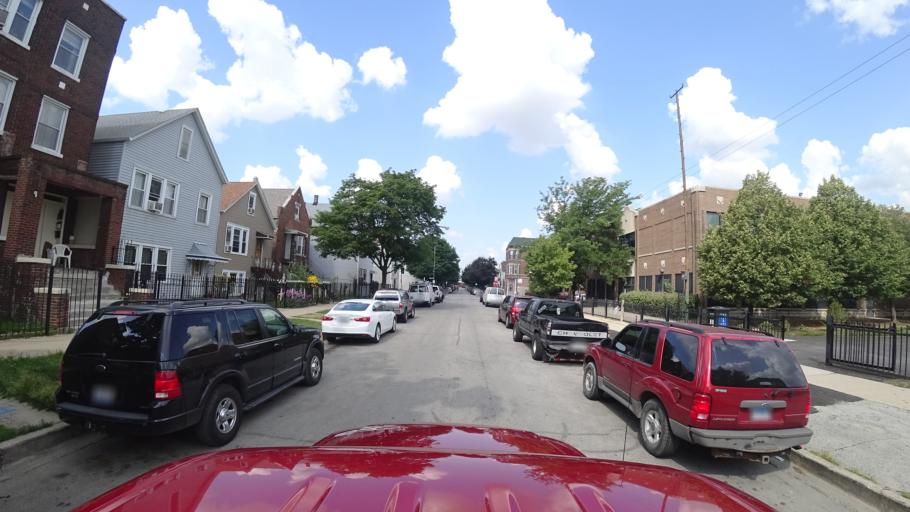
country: US
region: Illinois
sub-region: Cook County
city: Cicero
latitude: 41.8218
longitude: -87.7012
